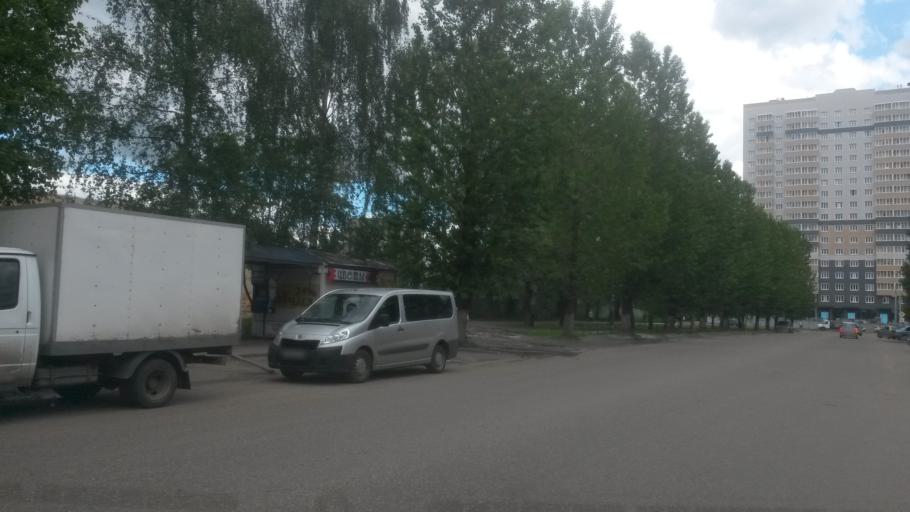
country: RU
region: Jaroslavl
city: Yaroslavl
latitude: 57.6854
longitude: 39.8029
